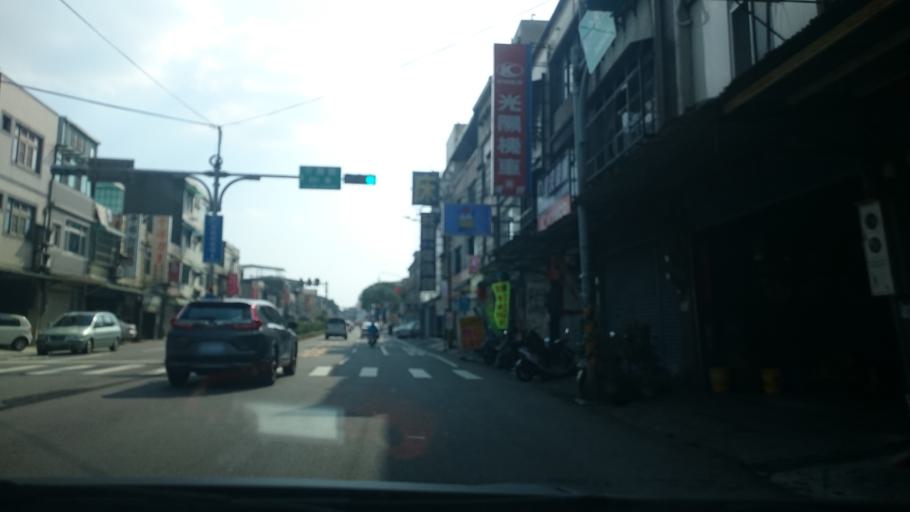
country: TW
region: Taiwan
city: Daxi
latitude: 24.9065
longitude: 121.2855
